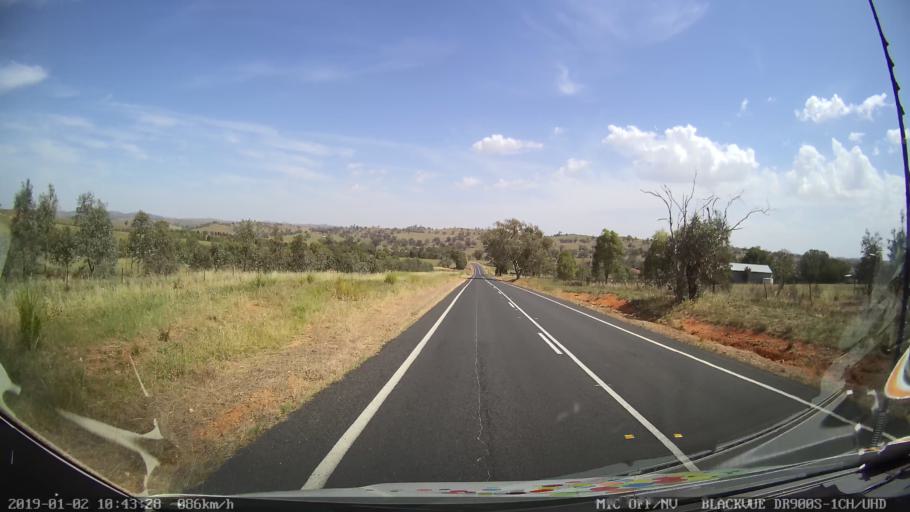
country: AU
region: New South Wales
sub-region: Cootamundra
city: Cootamundra
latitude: -34.7722
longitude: 148.3039
